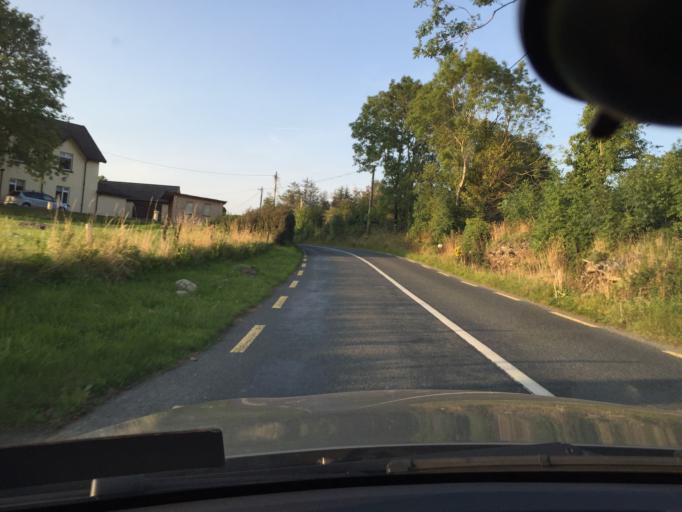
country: IE
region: Leinster
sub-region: Wicklow
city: Rathdrum
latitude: 53.0527
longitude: -6.2368
